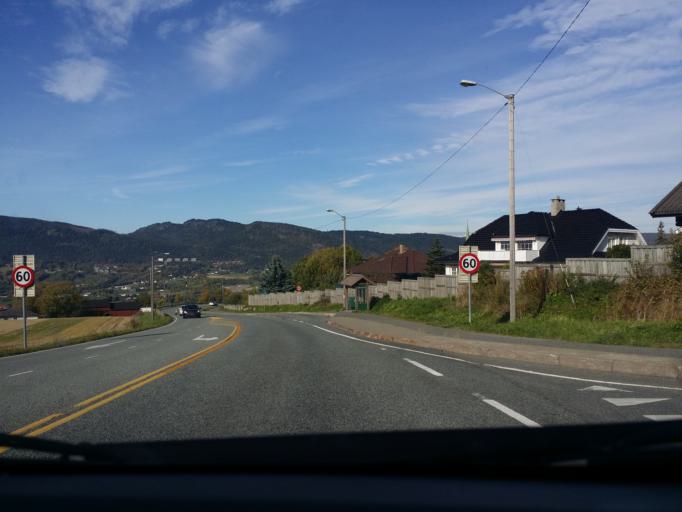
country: NO
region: Buskerud
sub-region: Lier
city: Tranby
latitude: 59.8085
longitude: 10.2609
